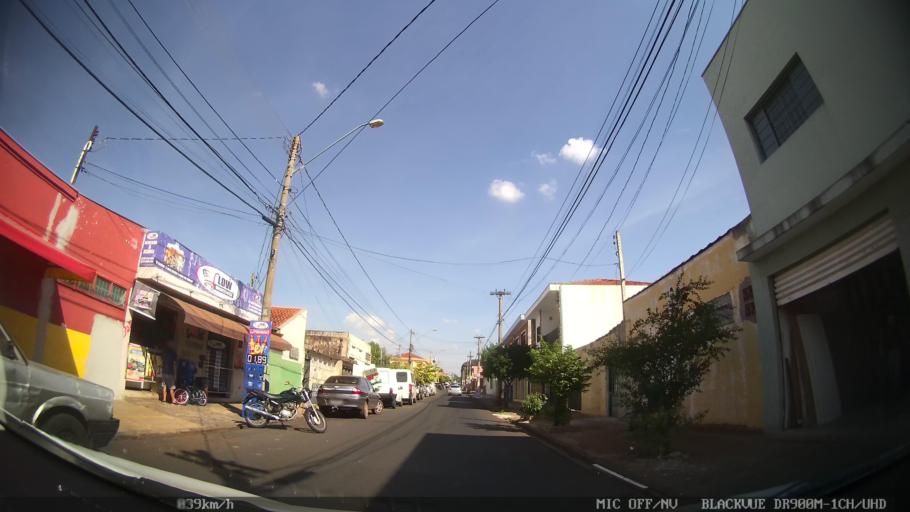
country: BR
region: Sao Paulo
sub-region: Ribeirao Preto
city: Ribeirao Preto
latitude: -21.1806
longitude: -47.8239
